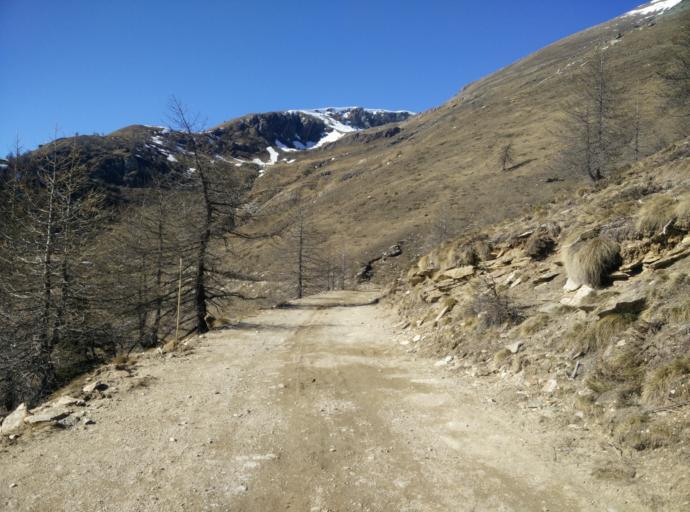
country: IT
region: Piedmont
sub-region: Provincia di Torino
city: Roure
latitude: 45.0450
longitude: 7.1120
